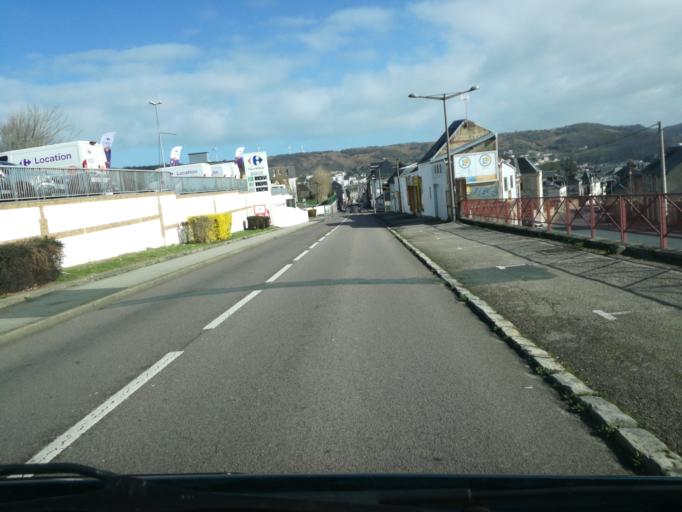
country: FR
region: Haute-Normandie
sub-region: Departement de la Seine-Maritime
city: Fecamp
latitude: 49.7533
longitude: 0.3721
